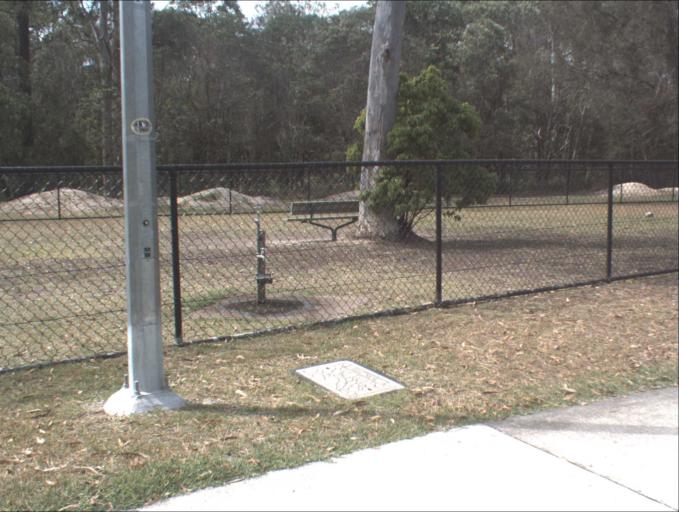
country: AU
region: Queensland
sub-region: Logan
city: Springwood
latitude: -27.6145
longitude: 153.1127
